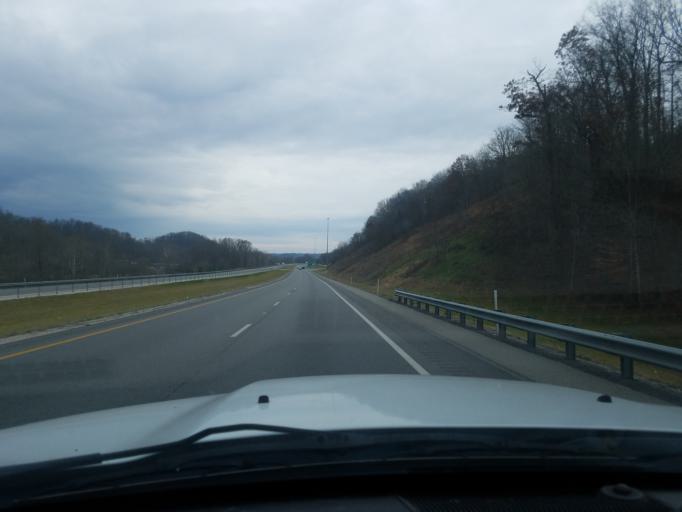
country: US
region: Kentucky
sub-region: Carter County
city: Grayson
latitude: 38.3547
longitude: -82.9065
